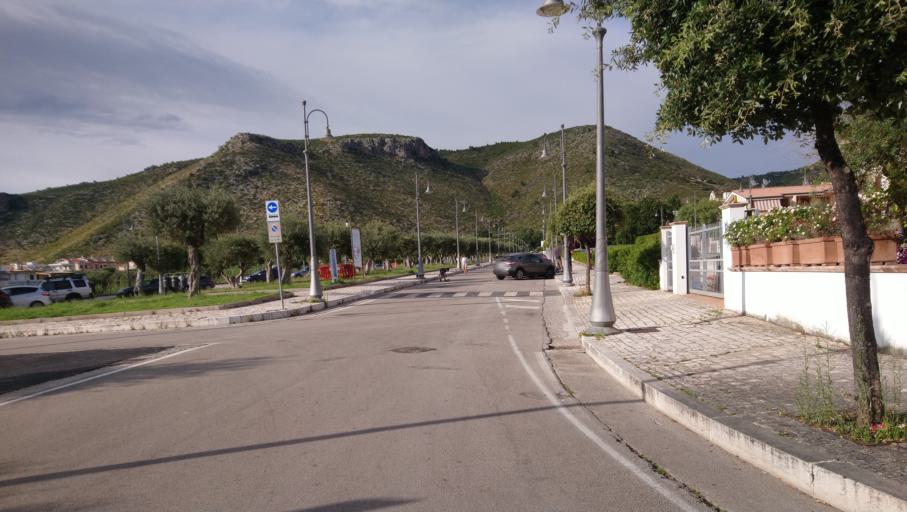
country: IT
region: Latium
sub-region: Provincia di Latina
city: Sperlonga
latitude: 41.2604
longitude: 13.4308
